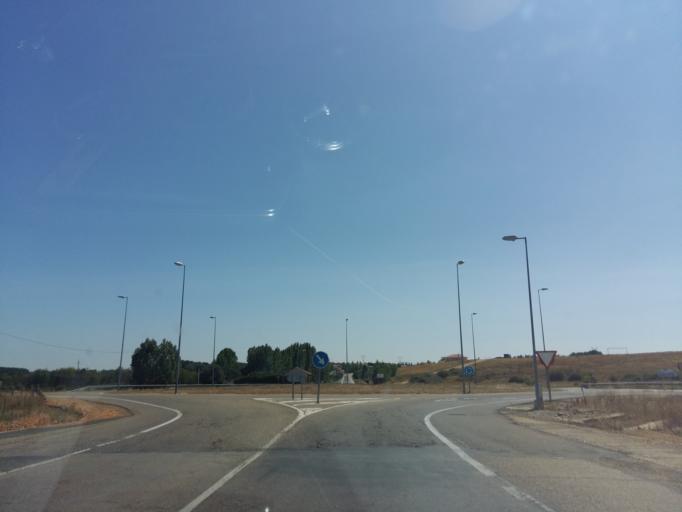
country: ES
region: Castille and Leon
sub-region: Provincia de Leon
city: San Justo de la Vega
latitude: 42.4360
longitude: -6.0332
